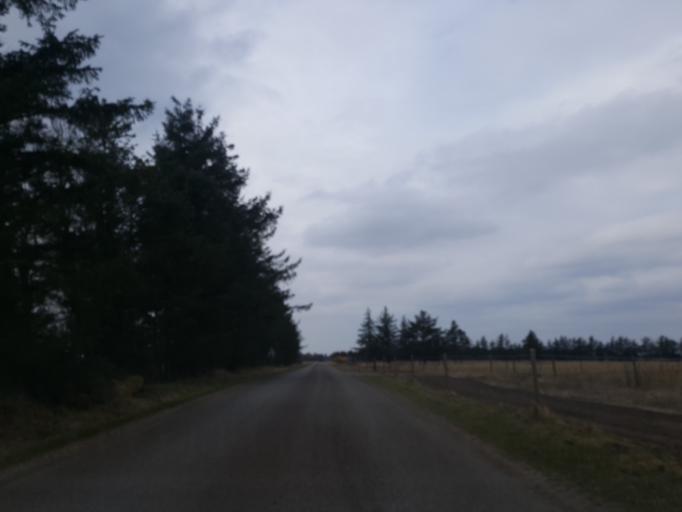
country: DK
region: Central Jutland
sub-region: Holstebro Kommune
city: Ulfborg
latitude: 56.3499
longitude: 8.2964
